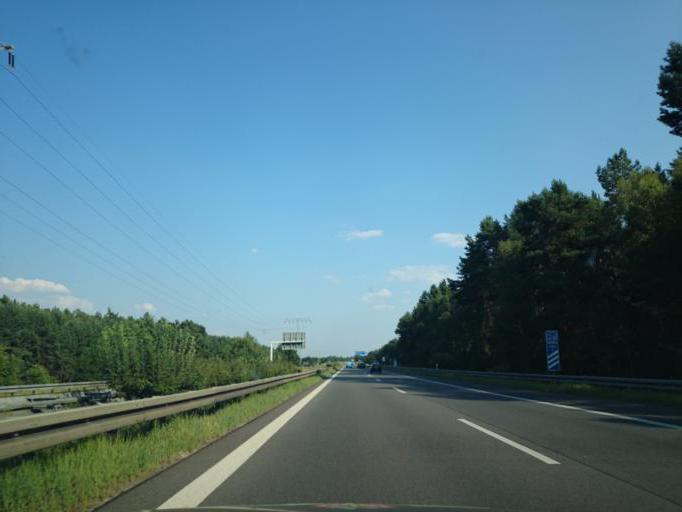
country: DE
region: Brandenburg
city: Velten
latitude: 52.6814
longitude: 13.2202
